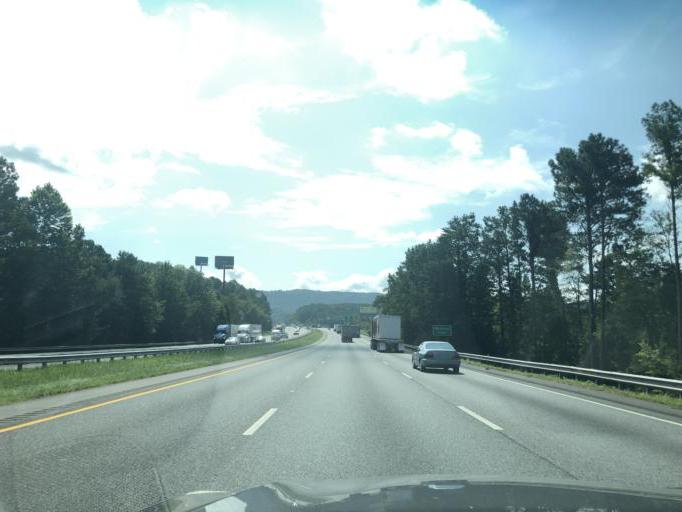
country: US
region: Georgia
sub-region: Whitfield County
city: Varnell
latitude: 34.8660
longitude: -85.0335
